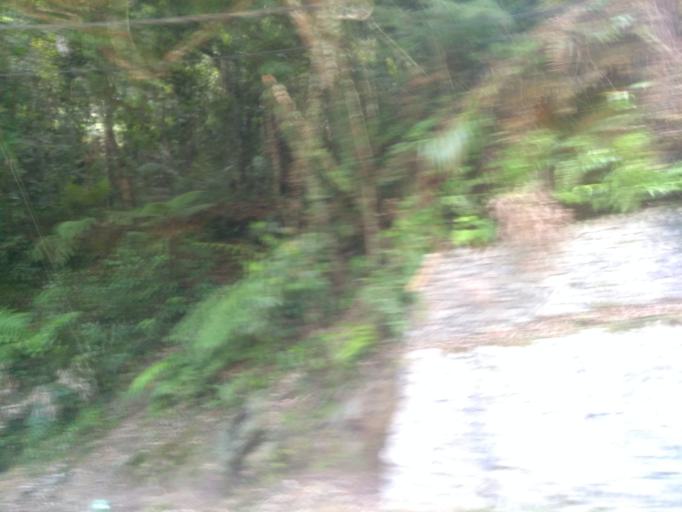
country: MY
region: Pahang
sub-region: Cameron Highlands
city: Tanah Rata
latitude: 4.4657
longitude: 101.3678
